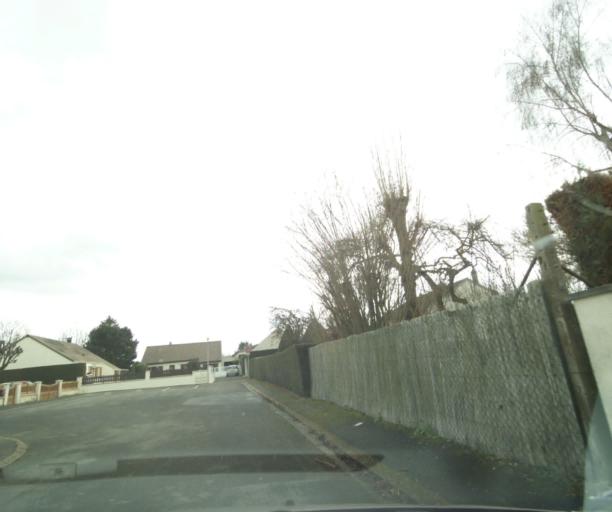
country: FR
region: Picardie
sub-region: Departement de l'Oise
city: Noyon
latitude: 49.5833
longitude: 2.9902
